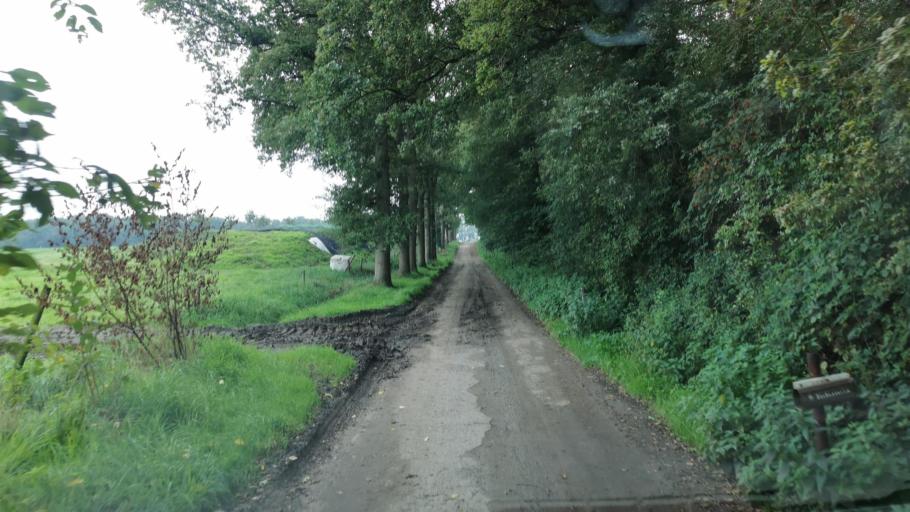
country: NL
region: Overijssel
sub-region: Gemeente Oldenzaal
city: Oldenzaal
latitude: 52.3301
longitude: 6.9958
